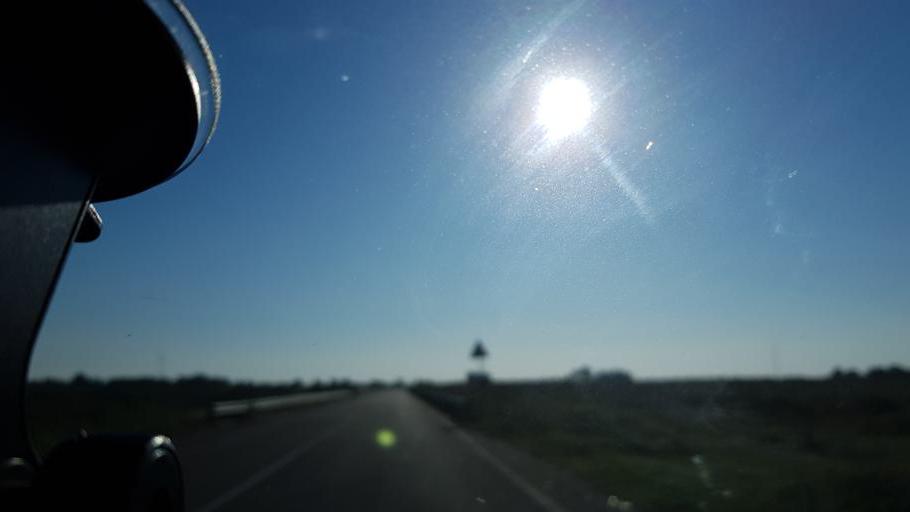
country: IT
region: Apulia
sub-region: Provincia di Lecce
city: Merine
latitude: 40.4081
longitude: 18.2556
